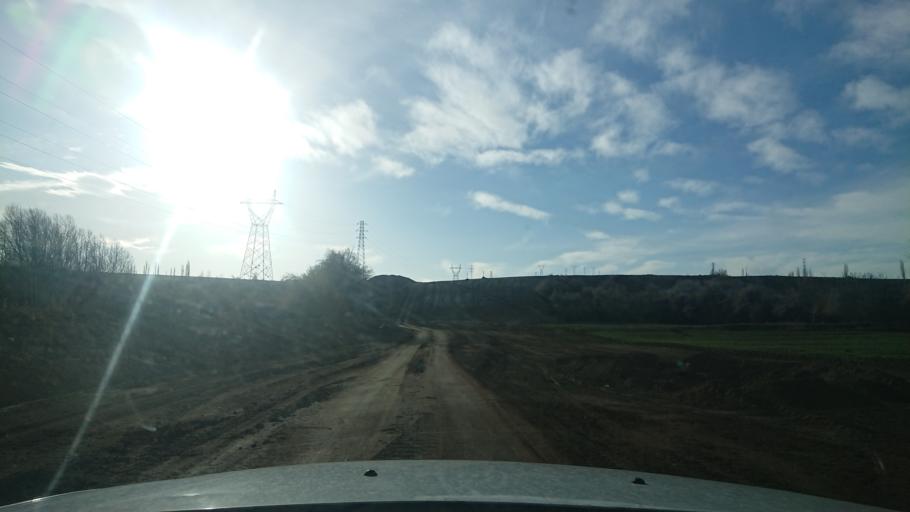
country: TR
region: Aksaray
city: Agacoren
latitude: 38.8602
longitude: 33.9420
